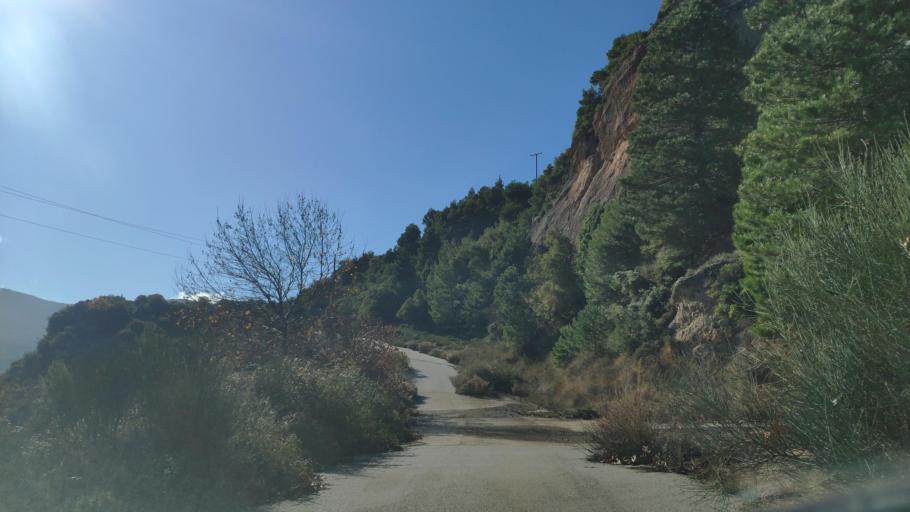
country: GR
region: West Greece
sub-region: Nomos Achaias
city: Aiyira
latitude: 38.0587
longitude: 22.4563
